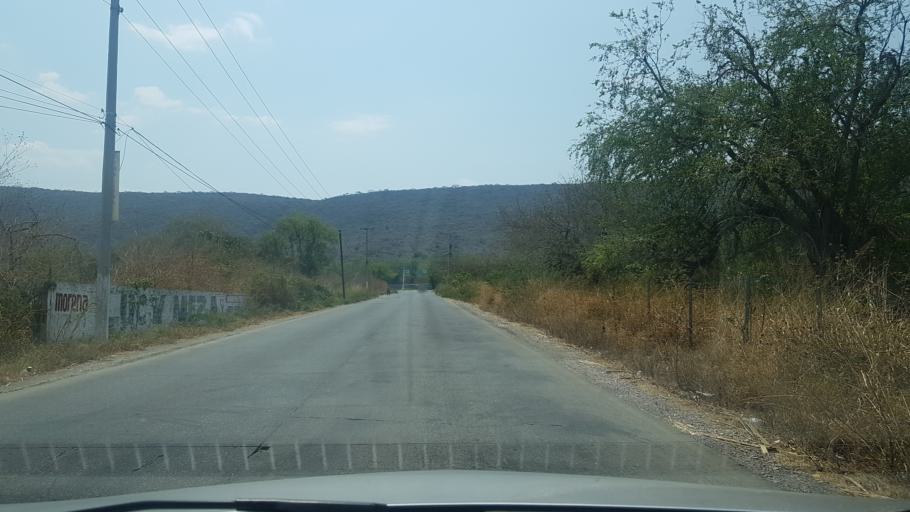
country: MX
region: Morelos
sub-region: Tlaltizapan de Zapata
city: Colonia Palo Prieto (Chipitongo)
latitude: 18.7298
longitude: -99.1221
